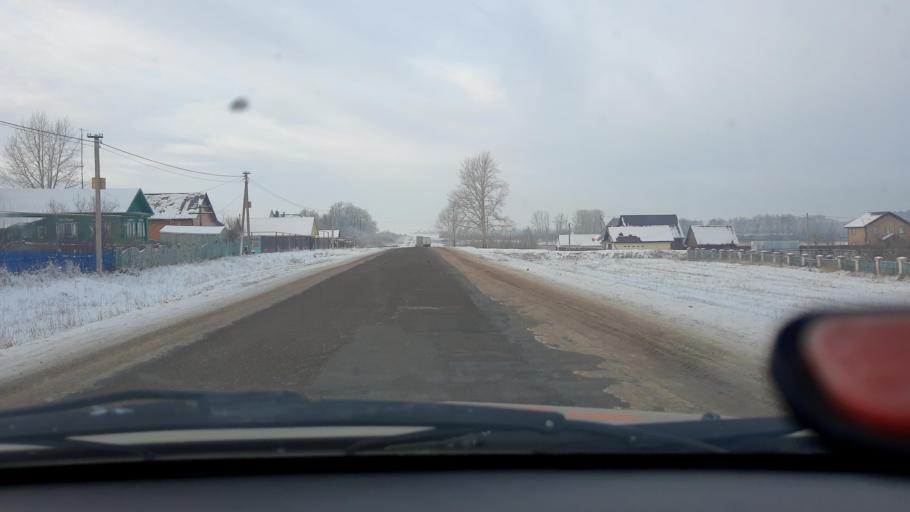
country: RU
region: Bashkortostan
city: Avdon
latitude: 54.3629
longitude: 55.8344
